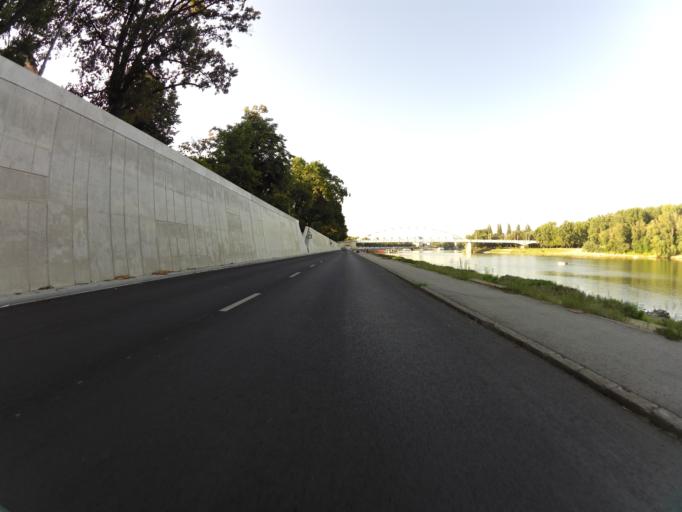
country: HU
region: Csongrad
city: Szeged
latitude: 46.2472
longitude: 20.1510
